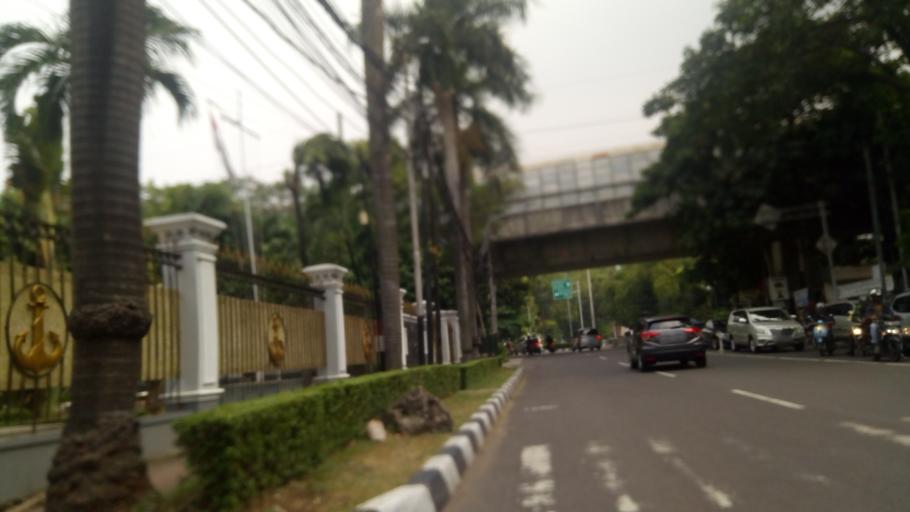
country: ID
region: Jakarta Raya
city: Jakarta
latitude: -6.1875
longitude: 106.8338
